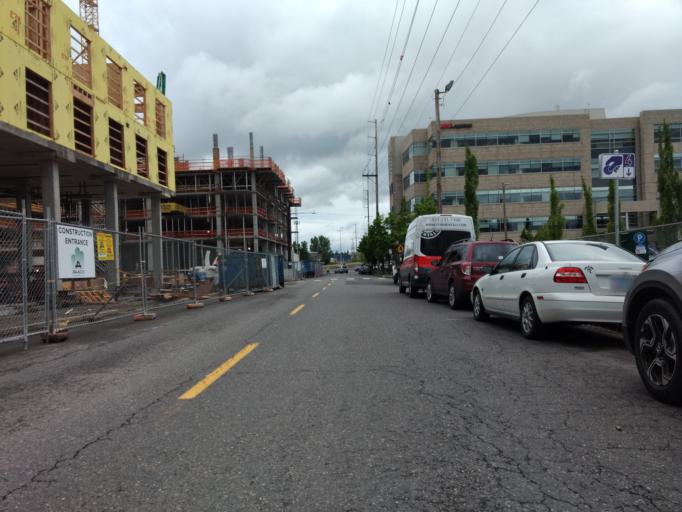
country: US
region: Oregon
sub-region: Multnomah County
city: Portland
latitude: 45.5345
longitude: -122.6947
